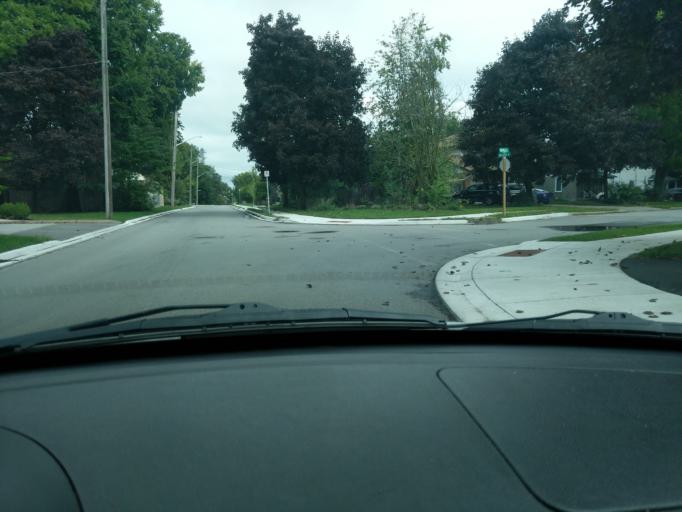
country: CA
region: Ontario
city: Cambridge
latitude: 43.4242
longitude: -80.3206
